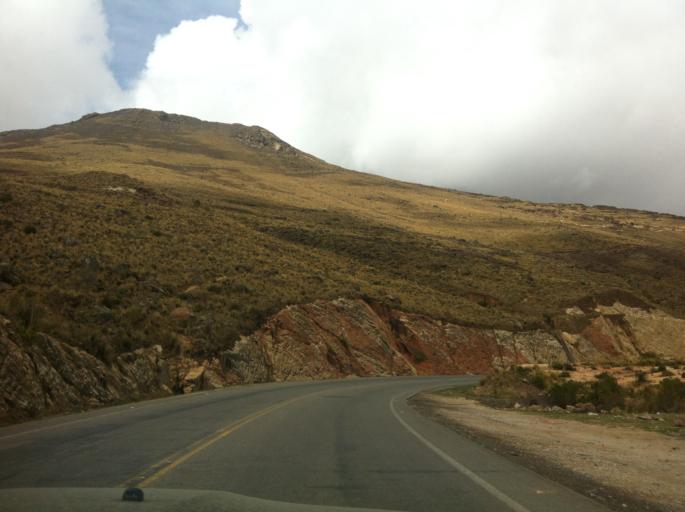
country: BO
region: Cochabamba
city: Irpa Irpa
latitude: -17.7013
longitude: -66.4817
